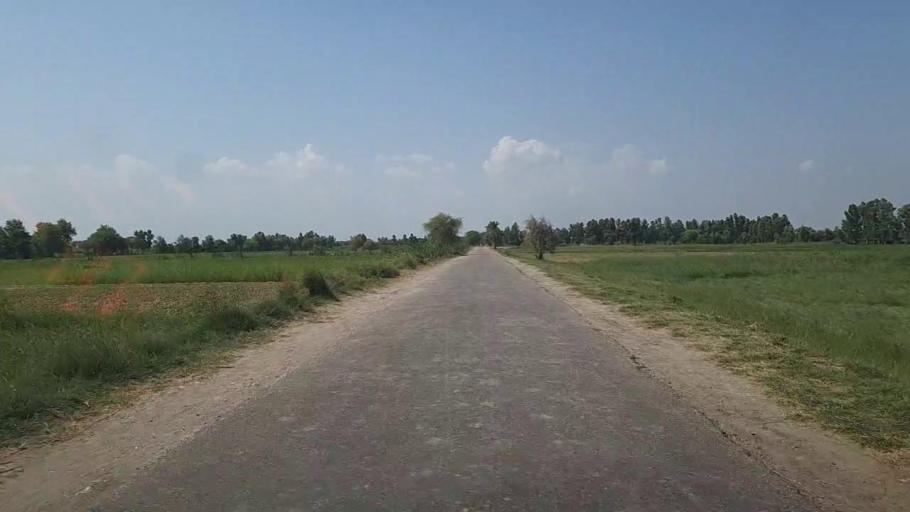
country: PK
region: Sindh
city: Khairpur
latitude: 28.0791
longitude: 69.6371
